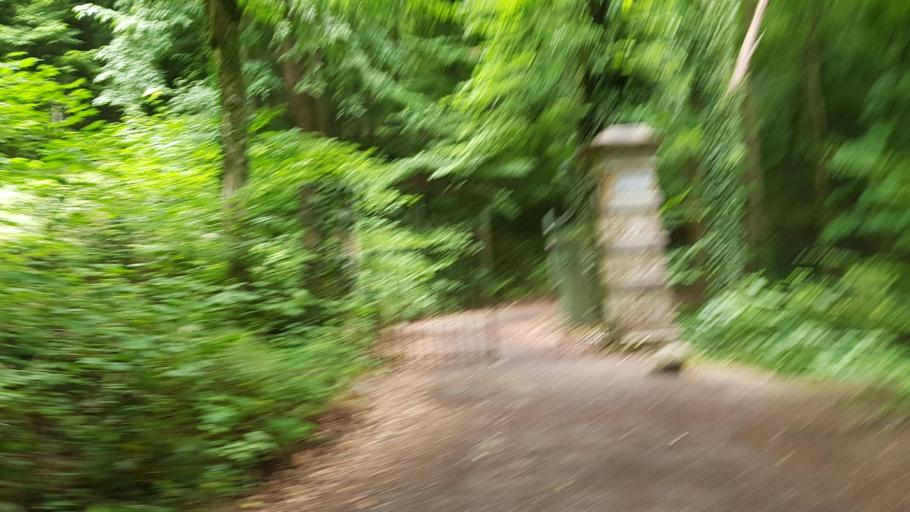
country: BE
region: Wallonia
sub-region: Province de Namur
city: Dinant
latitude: 50.2305
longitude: 4.9098
